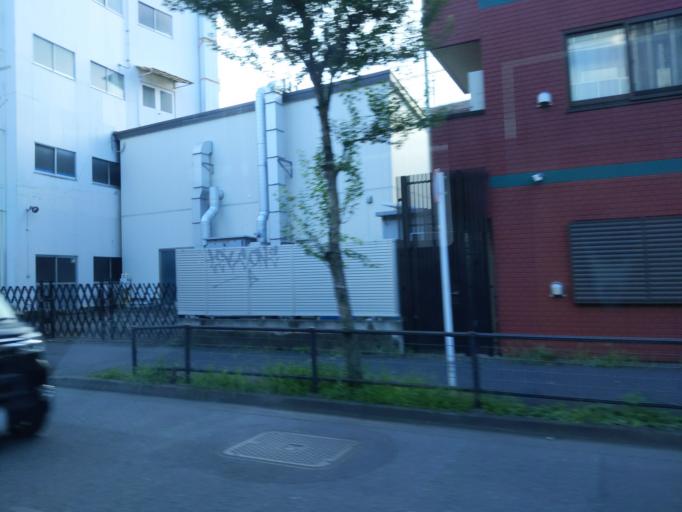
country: JP
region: Tokyo
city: Tokyo
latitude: 35.6268
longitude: 139.6938
